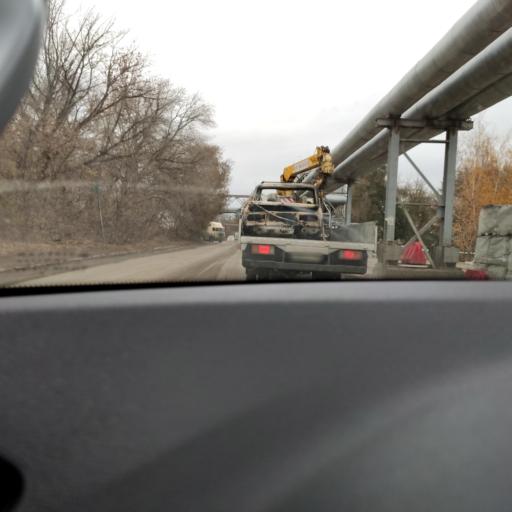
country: RU
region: Samara
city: Smyshlyayevka
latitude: 53.2055
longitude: 50.3016
